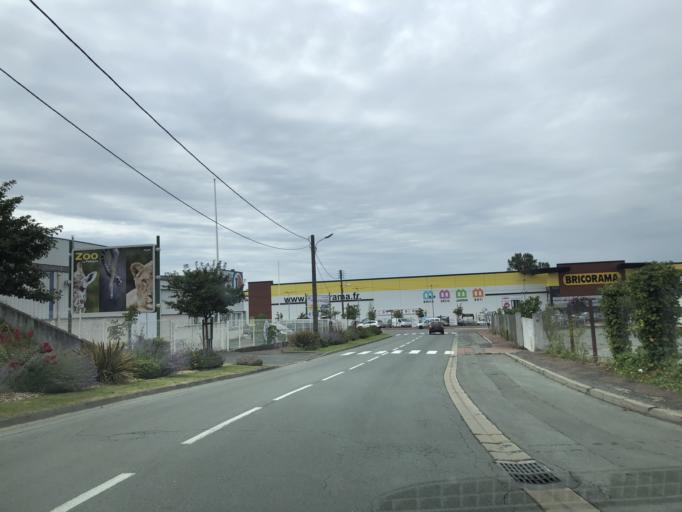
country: FR
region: Poitou-Charentes
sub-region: Departement de la Charente-Maritime
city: Saint-Georges-de-Didonne
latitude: 45.6306
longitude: -0.9961
